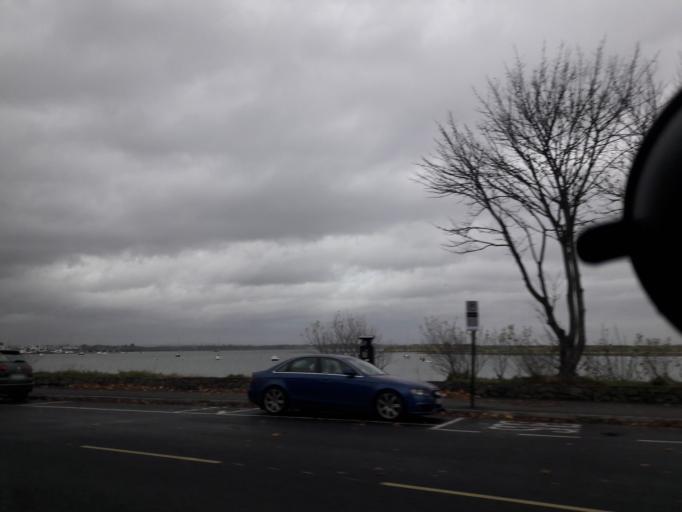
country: IE
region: Leinster
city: Malahide
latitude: 53.4510
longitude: -6.1452
